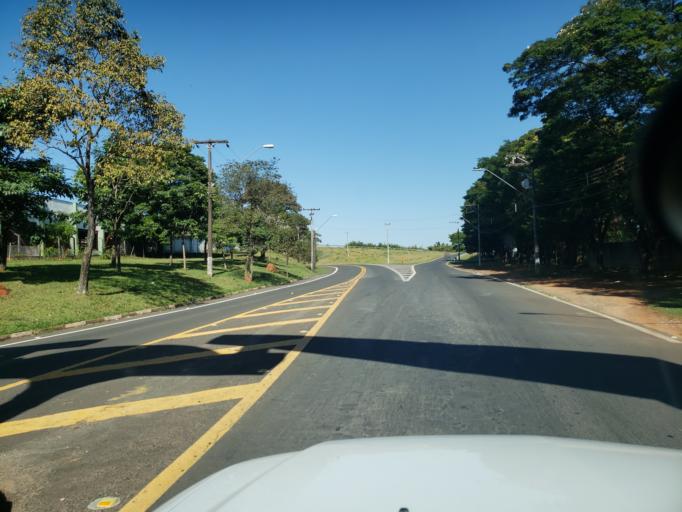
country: BR
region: Sao Paulo
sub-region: Itapira
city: Itapira
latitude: -22.4452
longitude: -46.8320
